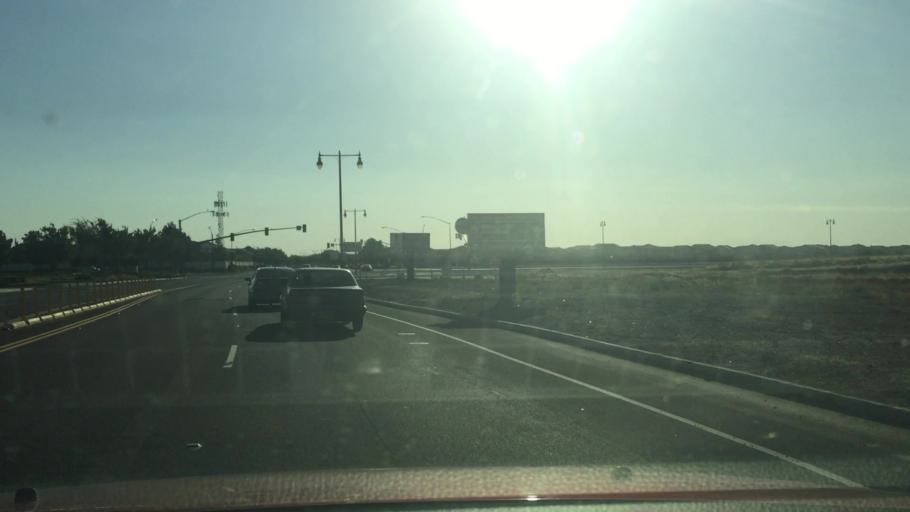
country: US
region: California
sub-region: San Joaquin County
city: Lathrop
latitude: 37.8119
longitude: -121.2980
